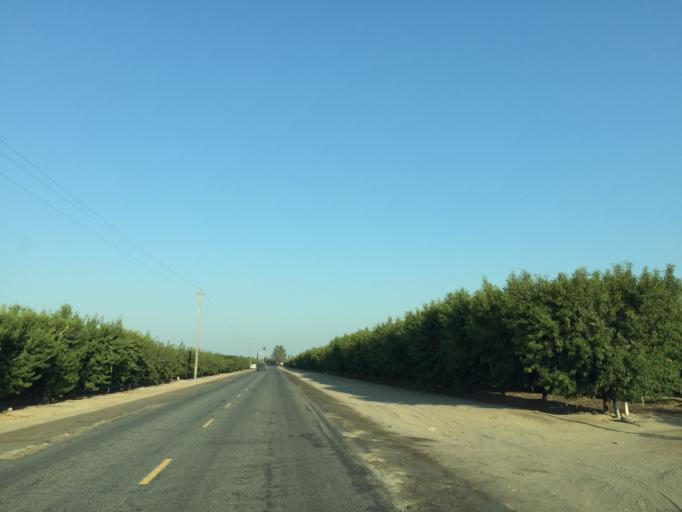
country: US
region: California
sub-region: Tulare County
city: London
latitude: 36.4589
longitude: -119.4677
